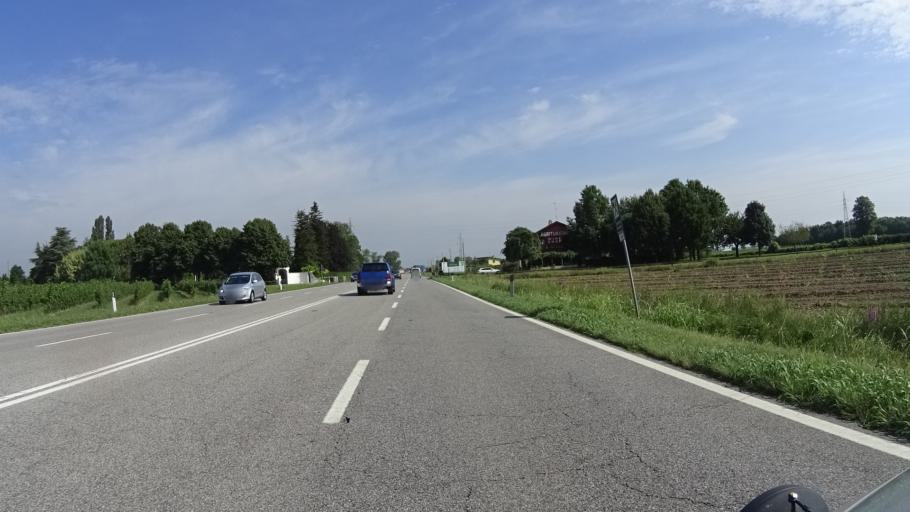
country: IT
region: Friuli Venezia Giulia
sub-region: Provincia di Udine
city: Latisana
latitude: 45.7777
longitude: 13.0219
